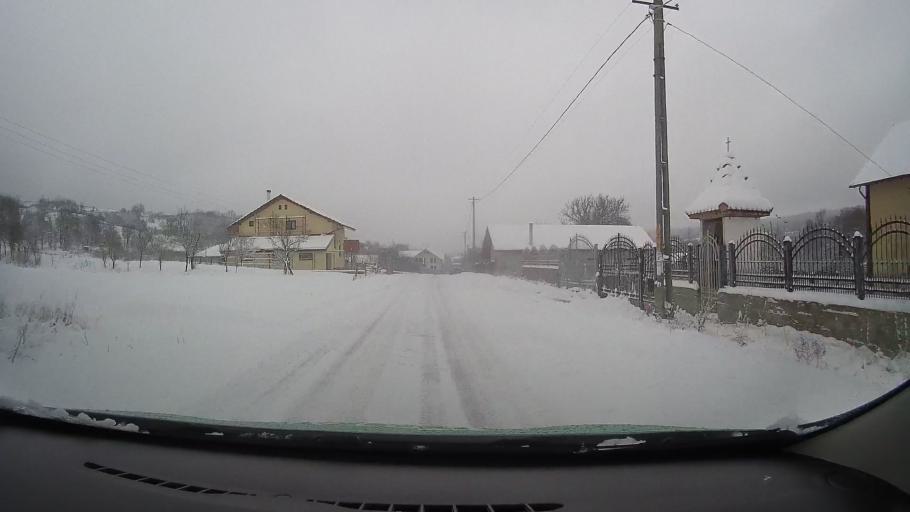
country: RO
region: Hunedoara
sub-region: Comuna Carjiti
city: Carjiti
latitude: 45.8299
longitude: 22.8450
